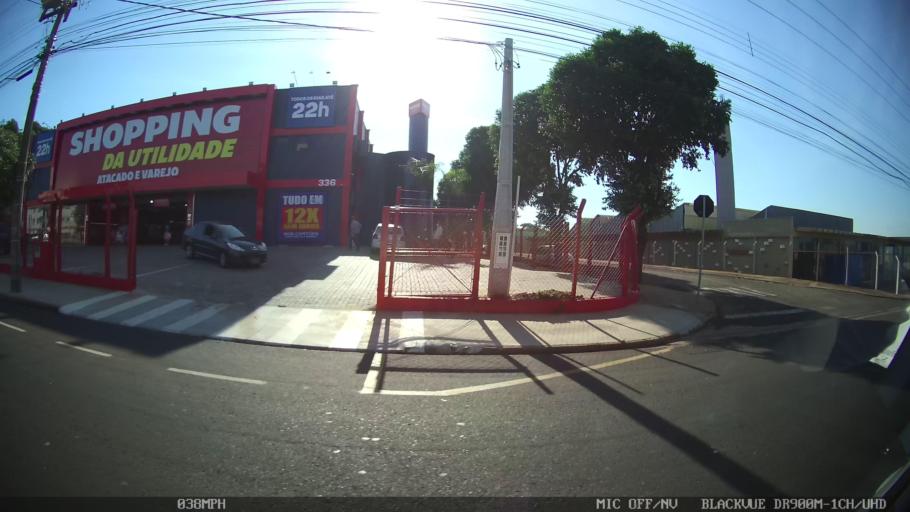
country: BR
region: Sao Paulo
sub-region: Sao Jose Do Rio Preto
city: Sao Jose do Rio Preto
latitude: -20.7874
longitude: -49.3555
